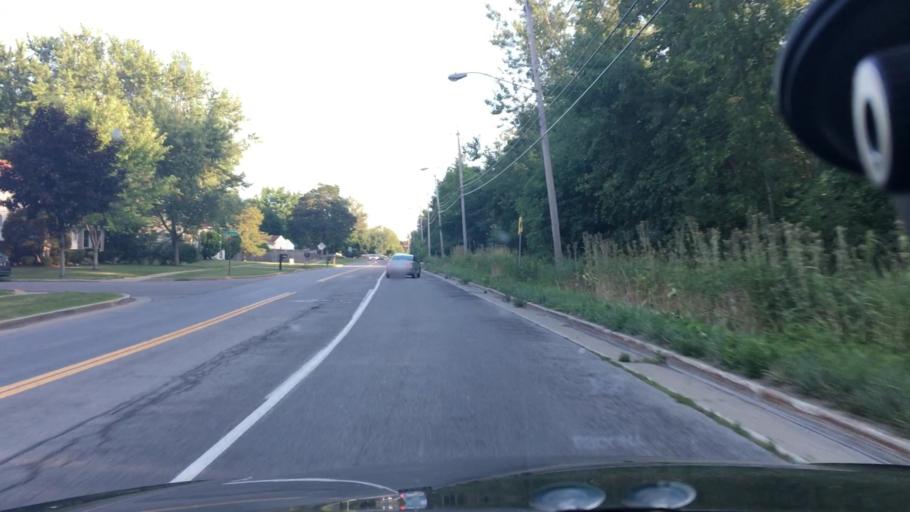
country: US
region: New York
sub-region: Erie County
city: Williamsville
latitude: 42.9986
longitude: -78.7610
